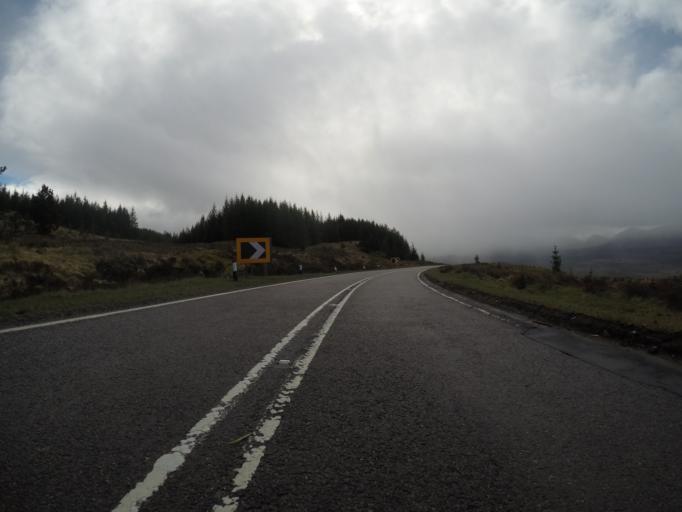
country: GB
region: Scotland
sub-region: Highland
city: Spean Bridge
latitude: 57.0861
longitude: -4.9621
